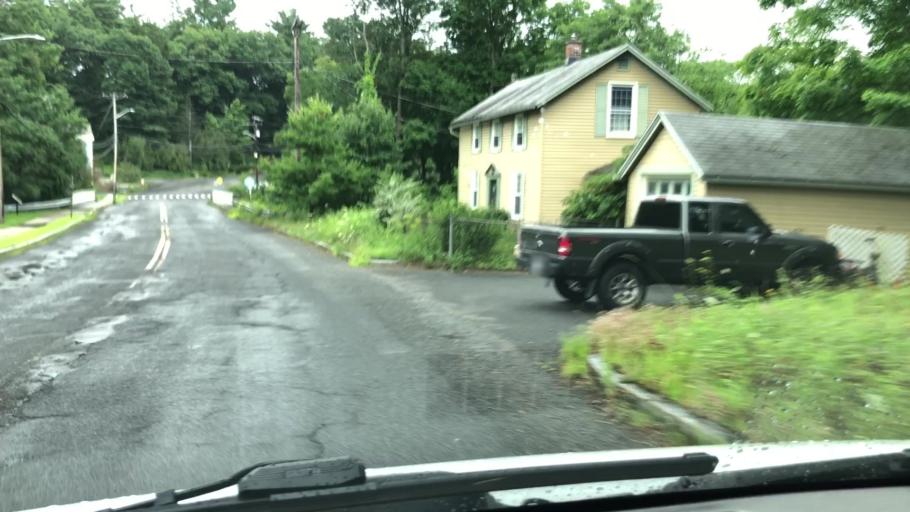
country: US
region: Massachusetts
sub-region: Hampshire County
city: Williamsburg
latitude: 42.3543
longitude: -72.7018
